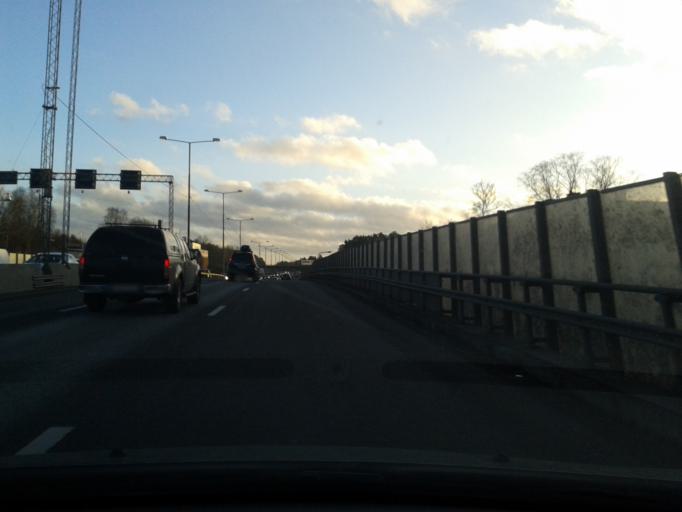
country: SE
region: Stockholm
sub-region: Stockholms Kommun
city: Arsta
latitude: 59.2795
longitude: 18.0914
